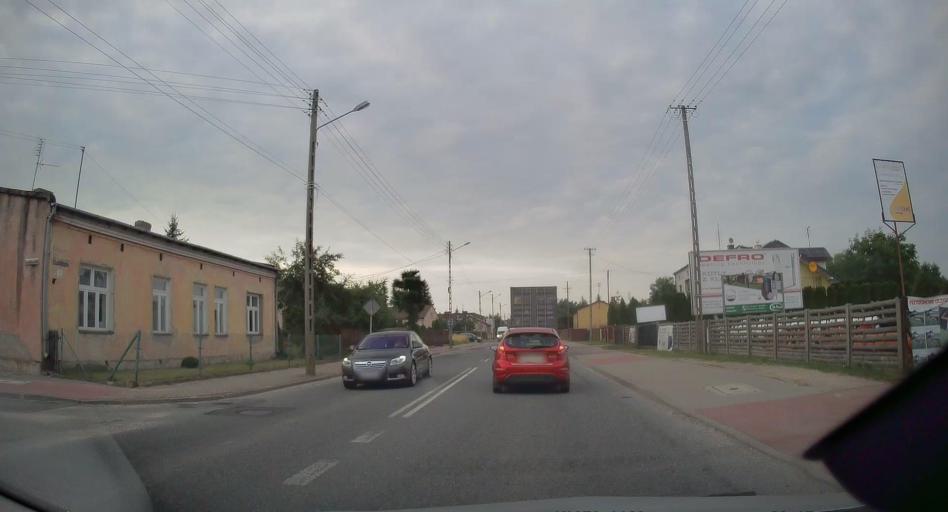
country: PL
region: Lodz Voivodeship
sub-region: Powiat radomszczanski
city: Kamiensk
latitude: 51.1960
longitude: 19.4990
